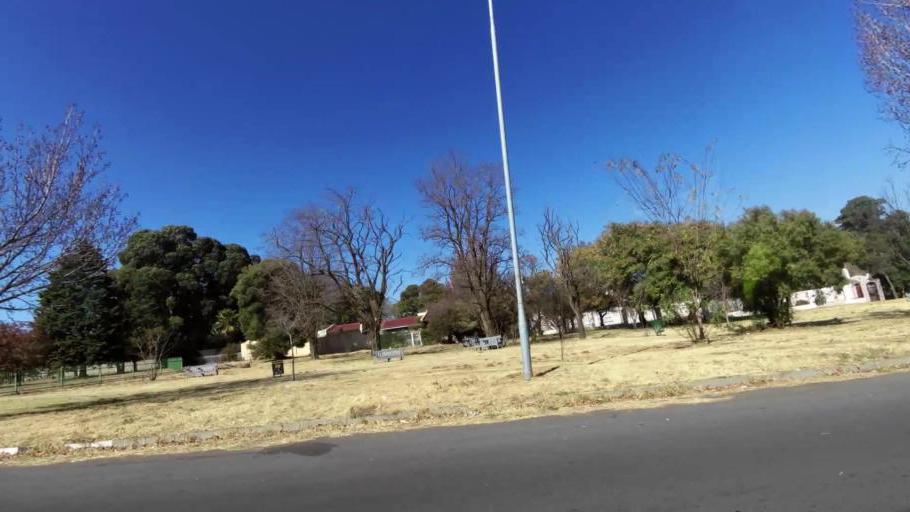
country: ZA
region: Gauteng
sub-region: City of Johannesburg Metropolitan Municipality
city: Johannesburg
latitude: -26.2469
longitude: 27.9939
